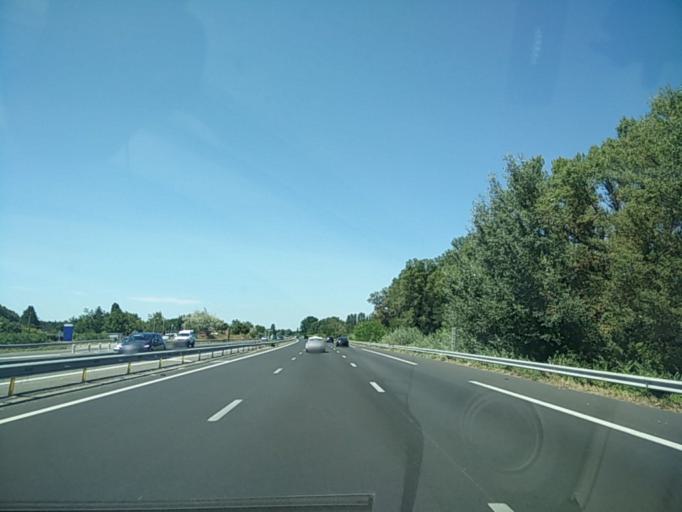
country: FR
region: Provence-Alpes-Cote d'Azur
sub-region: Departement du Vaucluse
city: Caumont-sur-Durance
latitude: 43.8764
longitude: 4.9425
